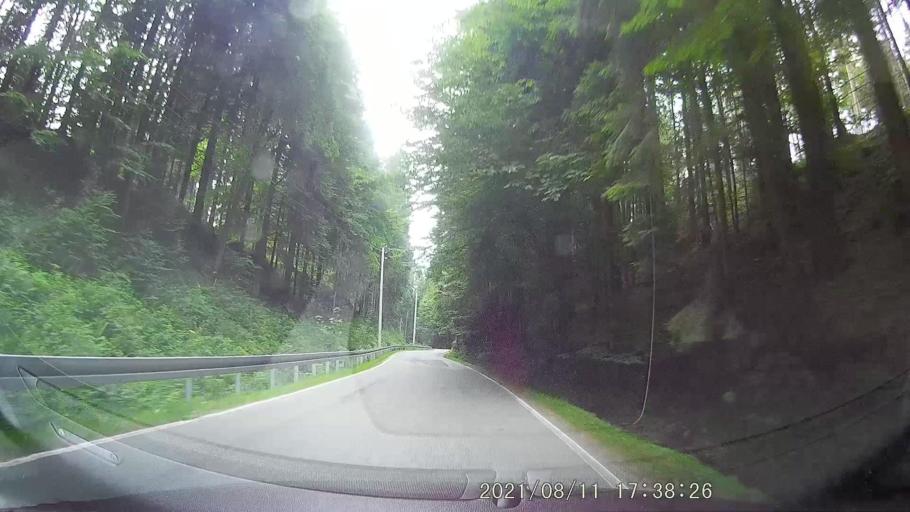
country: PL
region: Lower Silesian Voivodeship
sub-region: Powiat klodzki
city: Duszniki-Zdroj
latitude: 50.3439
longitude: 16.4016
